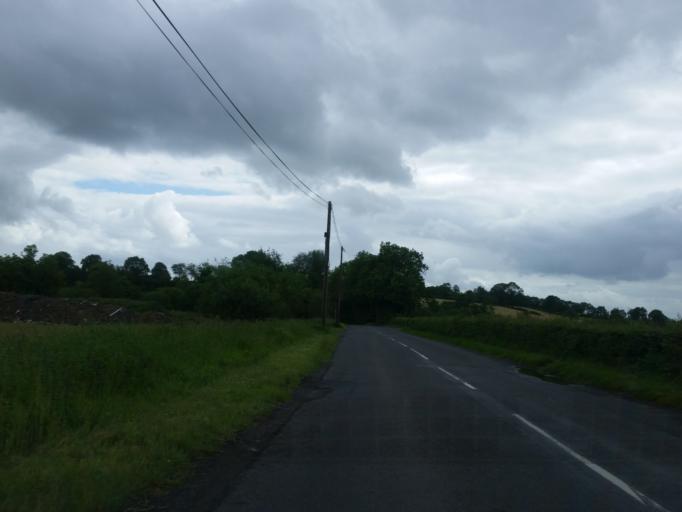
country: GB
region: Northern Ireland
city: Lisnaskea
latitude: 54.3002
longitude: -7.4174
